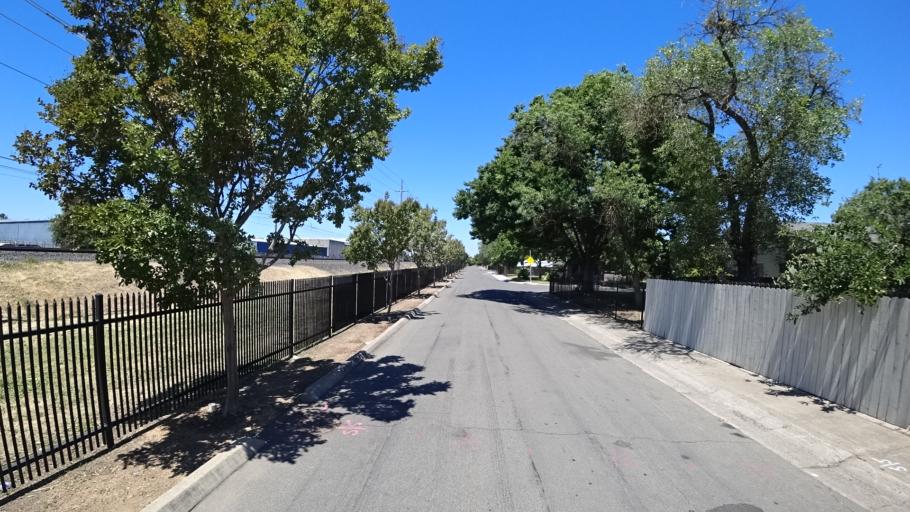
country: US
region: California
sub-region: Sacramento County
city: Parkway
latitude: 38.5307
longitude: -121.4813
